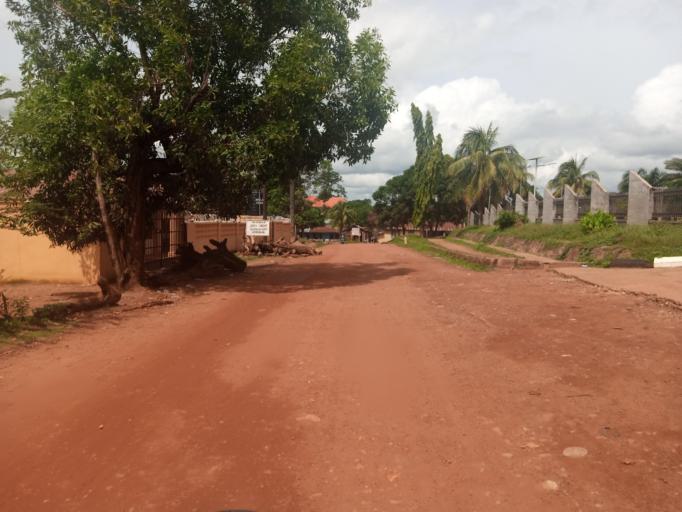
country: SL
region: Southern Province
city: Bo
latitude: 7.9674
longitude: -11.7435
